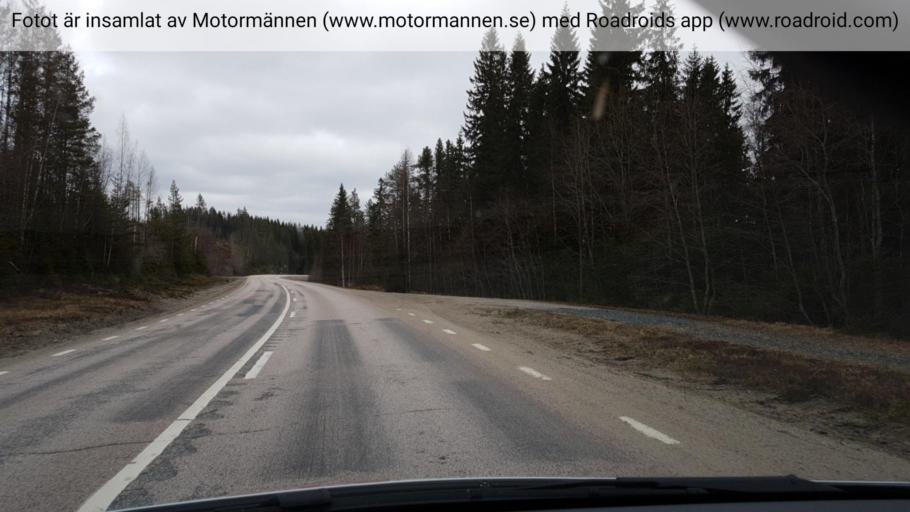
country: SE
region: Vaesternorrland
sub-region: OErnskoeldsviks Kommun
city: Ornskoldsvik
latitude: 63.4601
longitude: 18.5596
